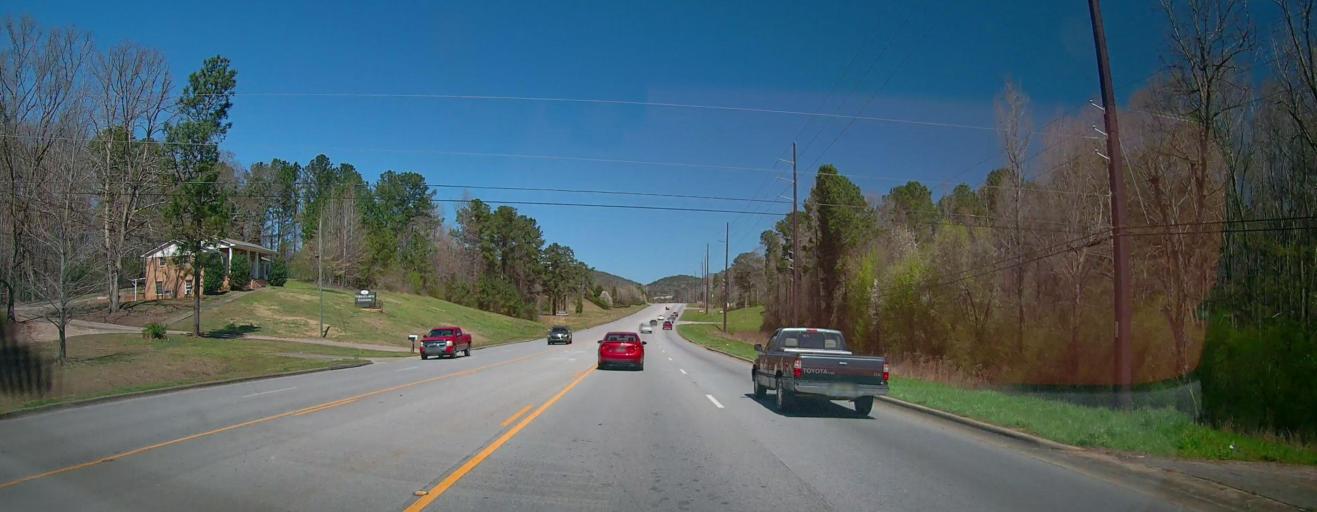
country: US
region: Alabama
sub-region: Calhoun County
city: Anniston
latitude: 33.6353
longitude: -85.7861
